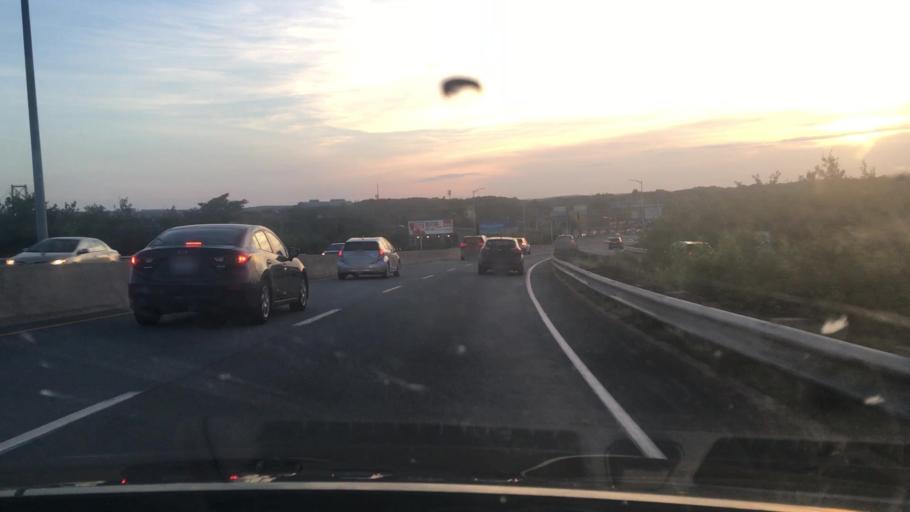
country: CA
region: Nova Scotia
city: Dartmouth
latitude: 44.6876
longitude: -63.5973
